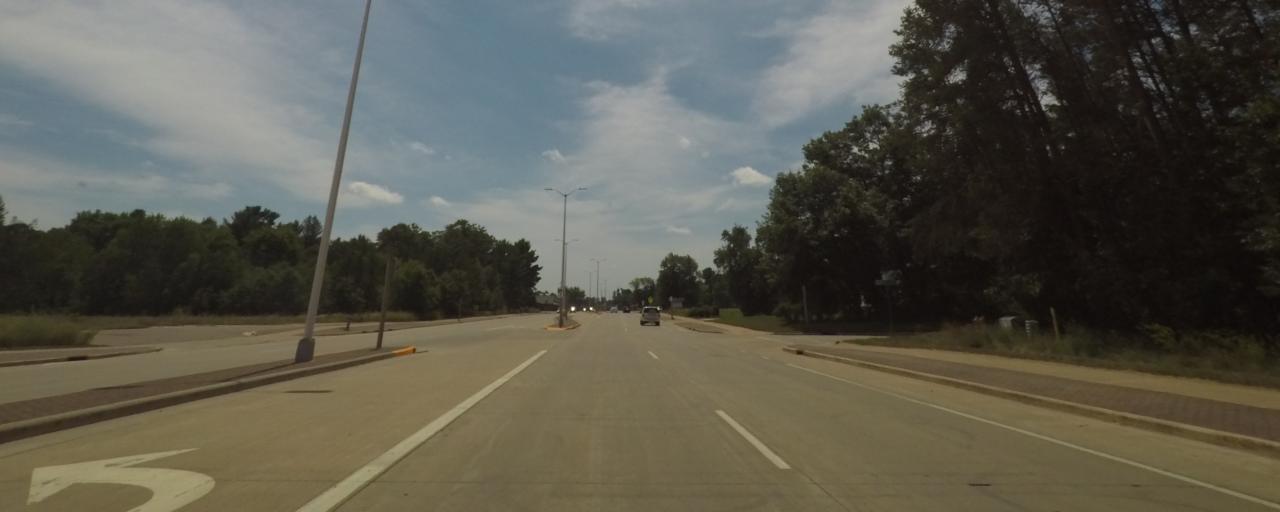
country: US
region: Wisconsin
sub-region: Portage County
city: Plover
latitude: 44.4677
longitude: -89.5461
